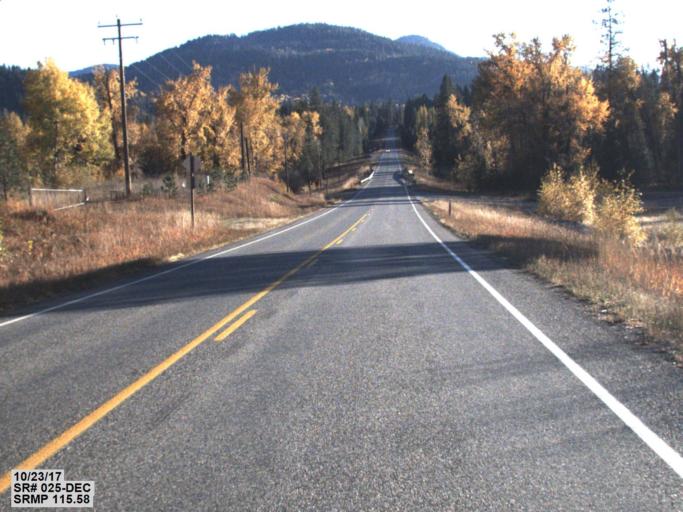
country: CA
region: British Columbia
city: Rossland
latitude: 48.9429
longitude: -117.7720
